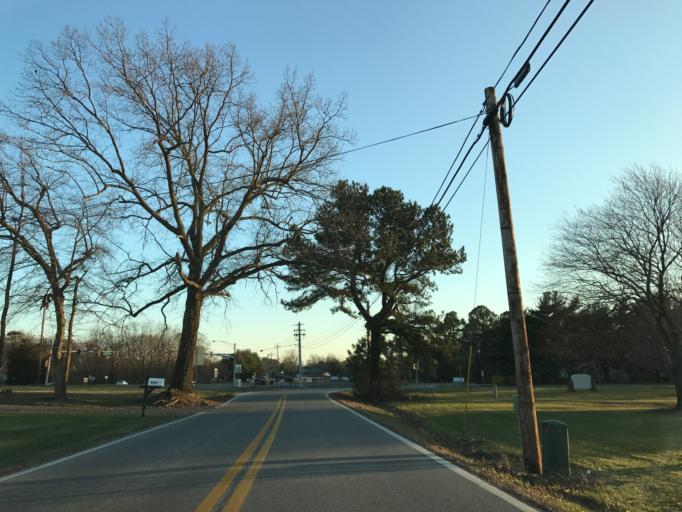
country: US
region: Maryland
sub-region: Talbot County
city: Easton
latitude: 38.7957
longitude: -76.0655
